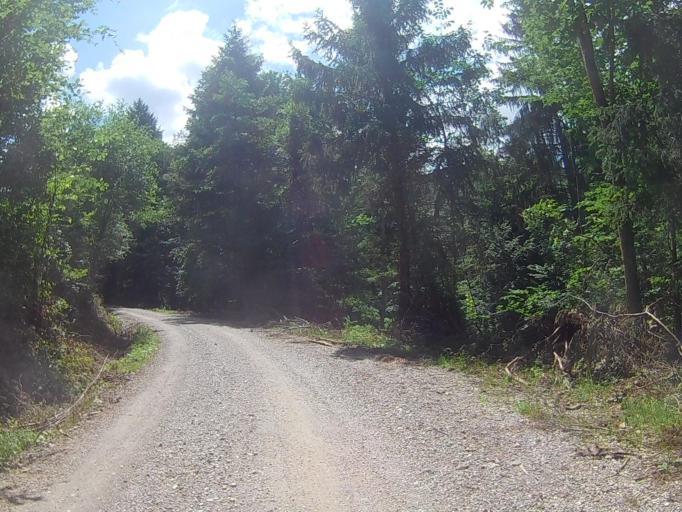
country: SI
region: Ruse
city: Ruse
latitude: 46.5265
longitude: 15.4981
